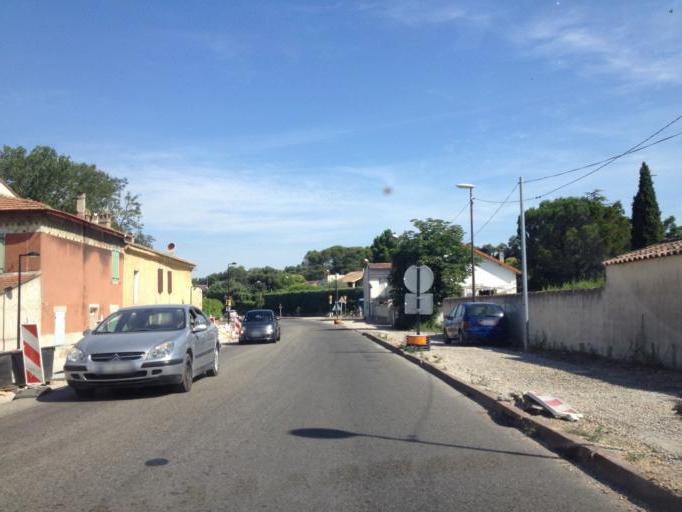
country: FR
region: Provence-Alpes-Cote d'Azur
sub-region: Departement du Vaucluse
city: Piolenc
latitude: 44.1791
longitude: 4.7598
